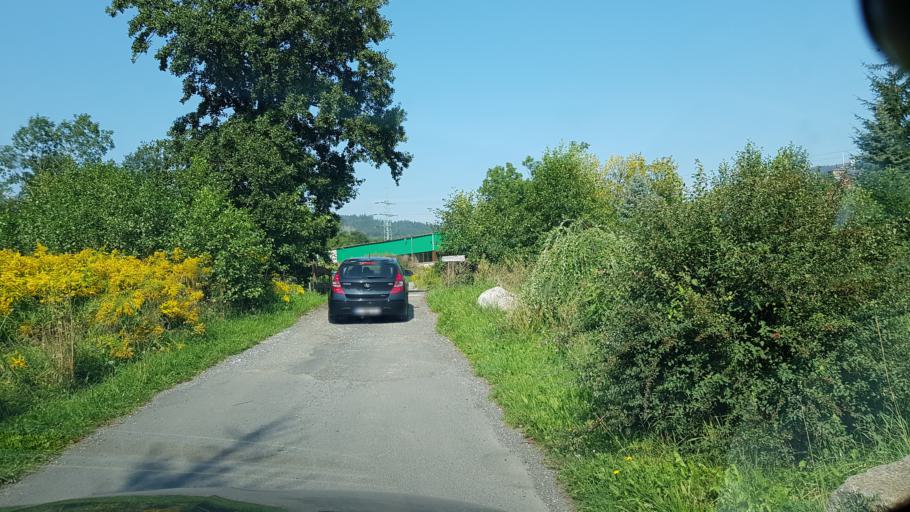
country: CZ
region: Olomoucky
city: Ceska Ves
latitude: 50.2644
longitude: 17.2410
